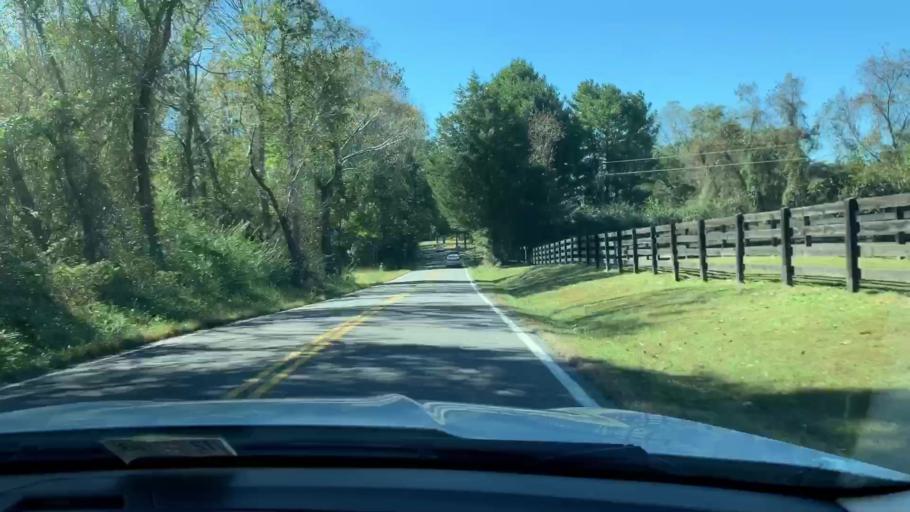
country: US
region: Virginia
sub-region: King William County
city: West Point
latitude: 37.4679
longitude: -76.8334
